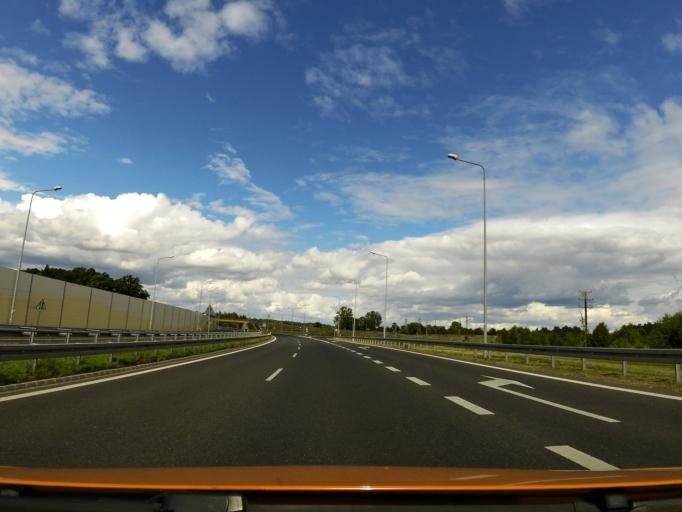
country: PL
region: West Pomeranian Voivodeship
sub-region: Powiat goleniowski
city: Nowogard
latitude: 53.6528
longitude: 15.0757
